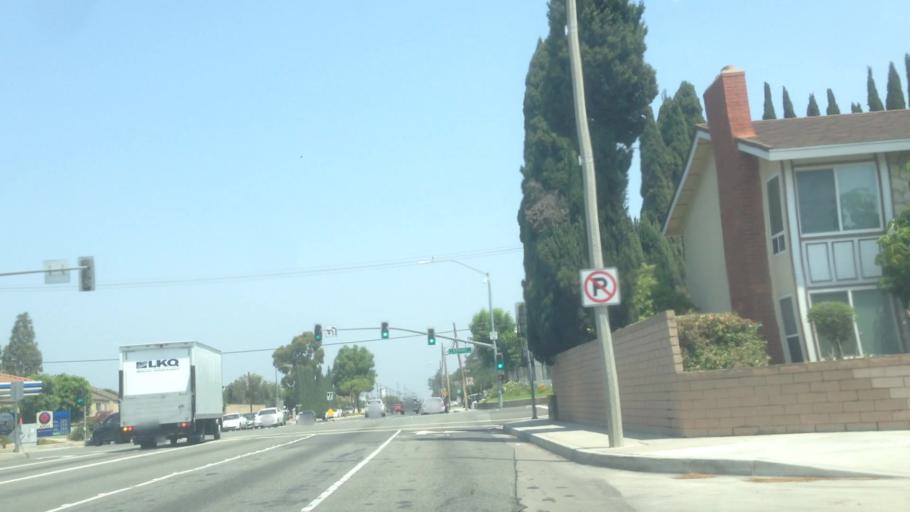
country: US
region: California
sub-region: Orange County
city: Fountain Valley
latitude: 33.7305
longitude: -117.9372
